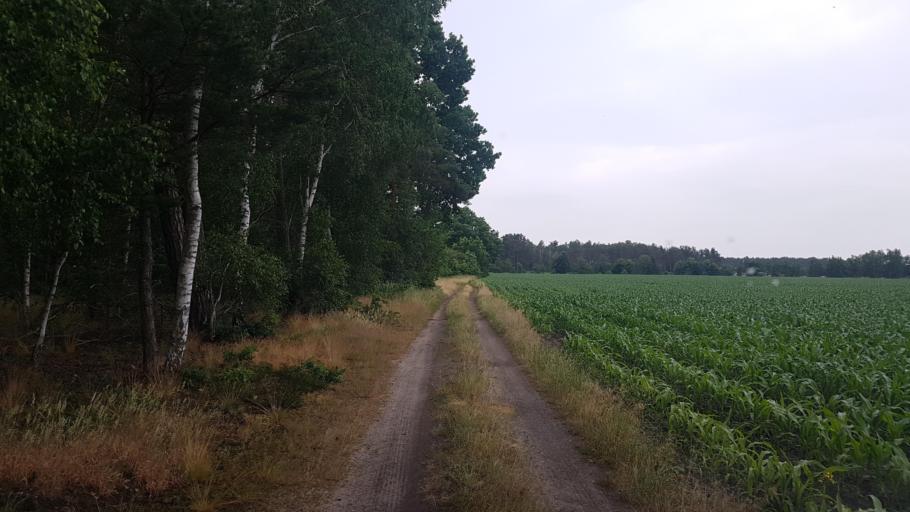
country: DE
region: Brandenburg
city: Schilda
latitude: 51.6407
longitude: 13.3868
